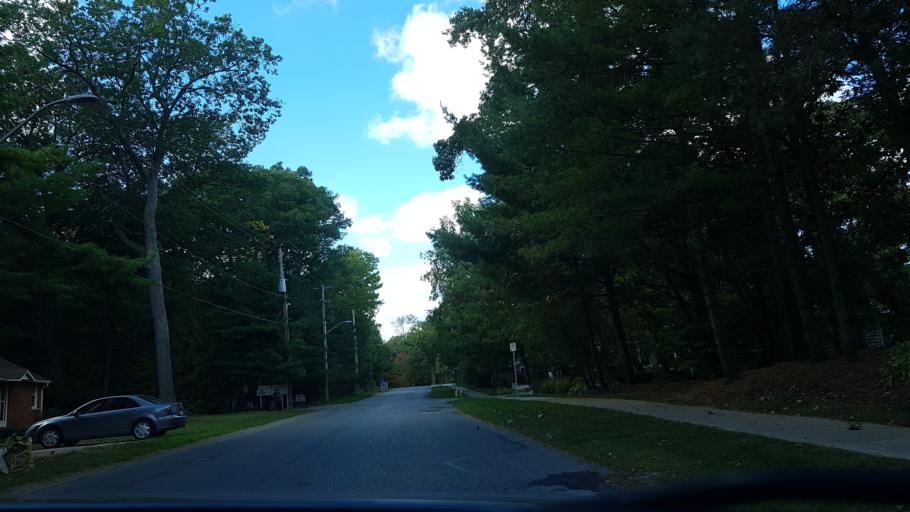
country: CA
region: Ontario
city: Lambton Shores
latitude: 43.3106
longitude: -81.7632
